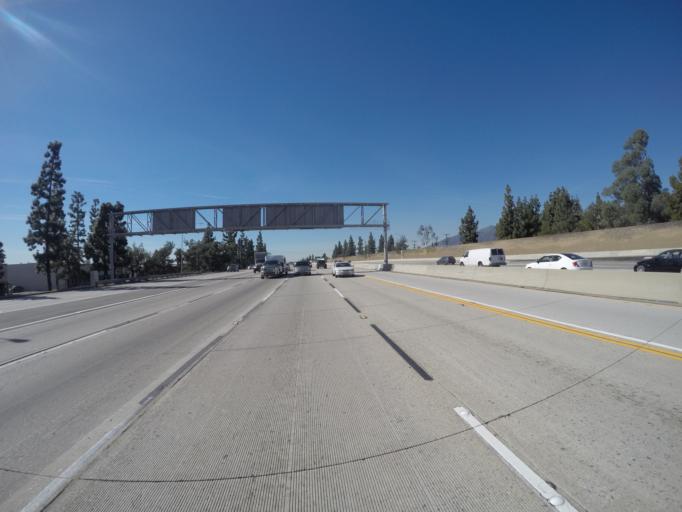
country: US
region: California
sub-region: Los Angeles County
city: Bradbury
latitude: 34.1355
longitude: -117.9637
